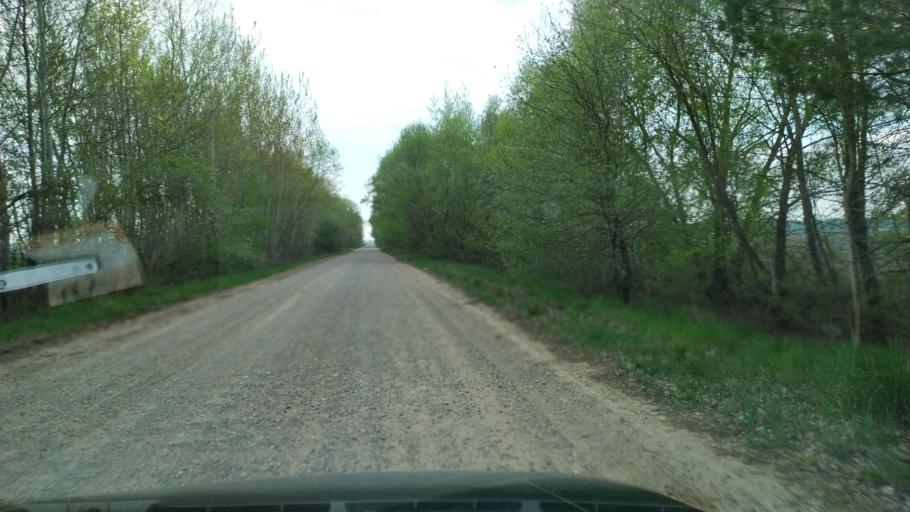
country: BY
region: Brest
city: Zhabinka
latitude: 52.1408
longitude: 24.0918
